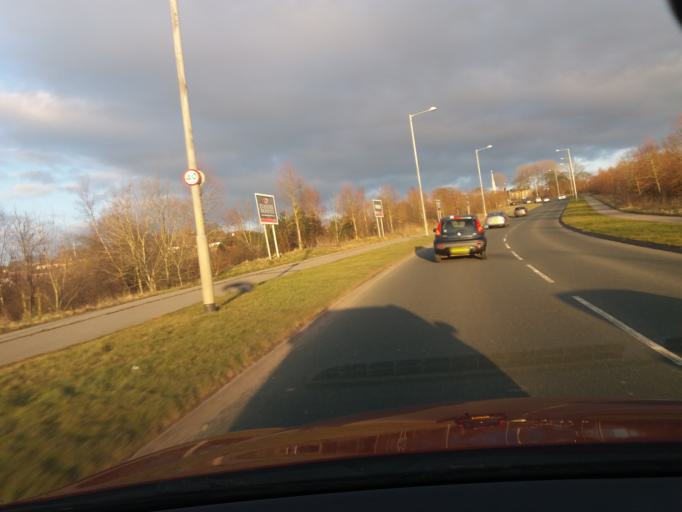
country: GB
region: England
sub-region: Lancashire
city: Chorley
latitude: 53.6733
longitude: -2.6401
